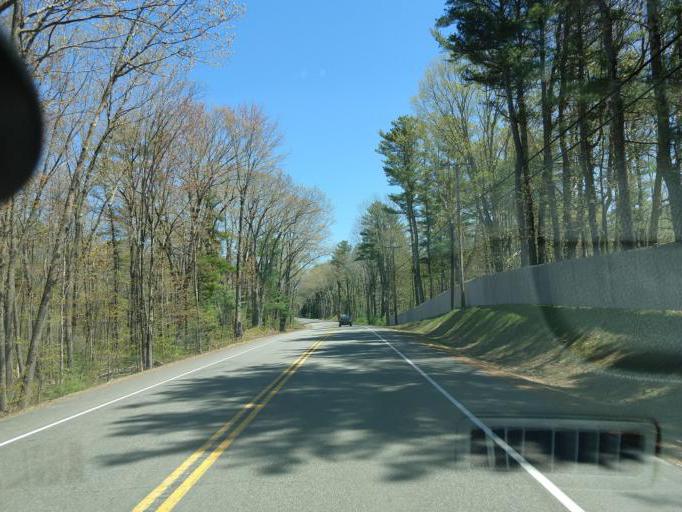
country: US
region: Maine
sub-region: York County
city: York Harbor
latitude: 43.1427
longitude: -70.6869
